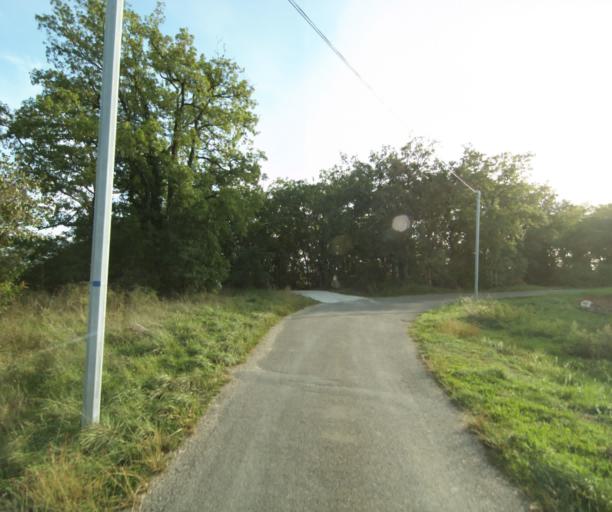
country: FR
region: Midi-Pyrenees
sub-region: Departement du Gers
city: Gondrin
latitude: 43.9026
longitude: 0.2780
